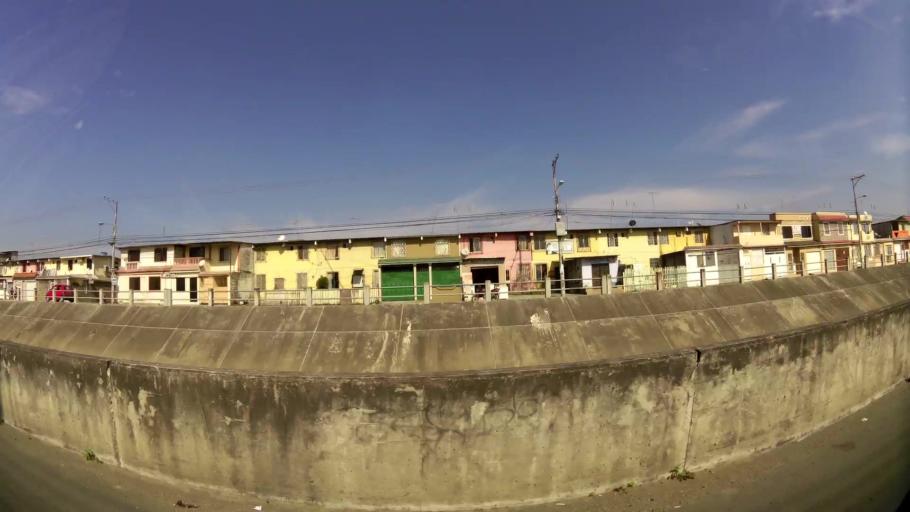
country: EC
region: Guayas
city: Eloy Alfaro
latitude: -2.0907
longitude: -79.9181
